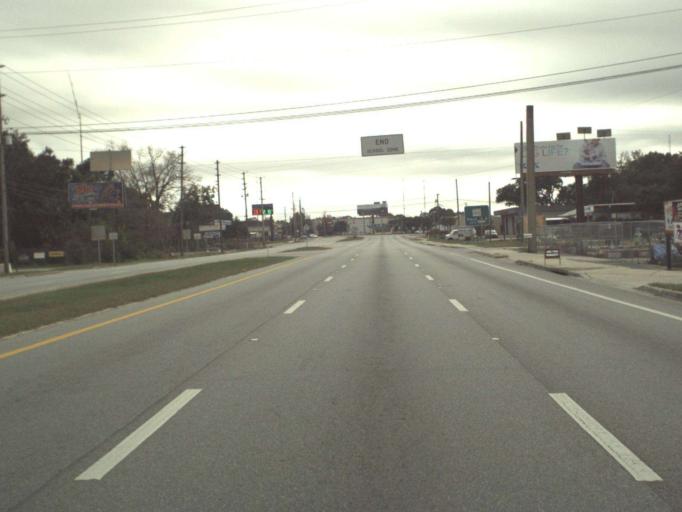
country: US
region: Florida
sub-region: Escambia County
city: Brent
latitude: 30.4622
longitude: -87.2408
